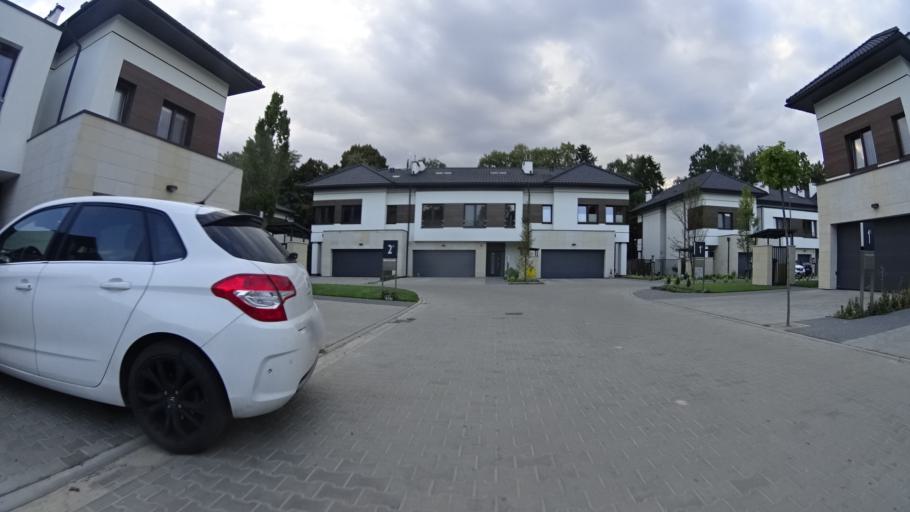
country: PL
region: Masovian Voivodeship
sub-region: Powiat warszawski zachodni
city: Ozarow Mazowiecki
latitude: 52.2326
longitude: 20.8064
